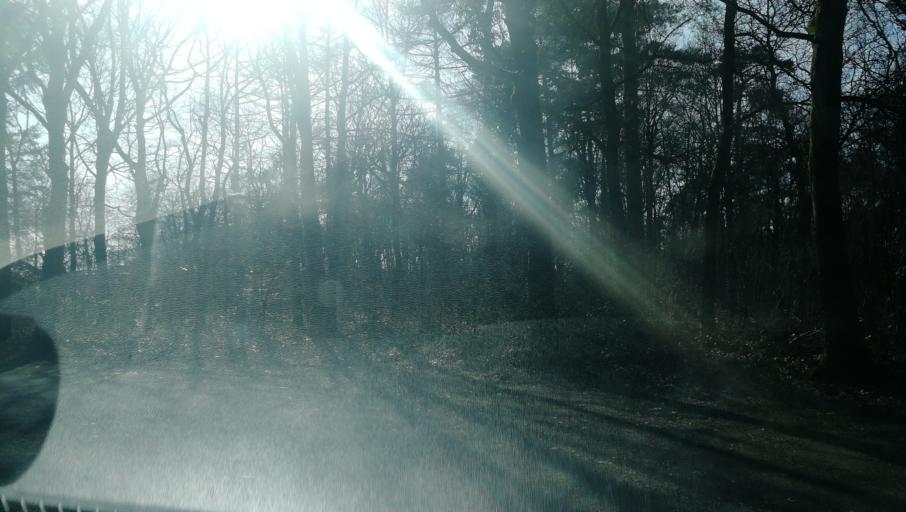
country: NL
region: Limburg
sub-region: Gemeente Venlo
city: Venlo
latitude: 51.3427
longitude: 6.1835
